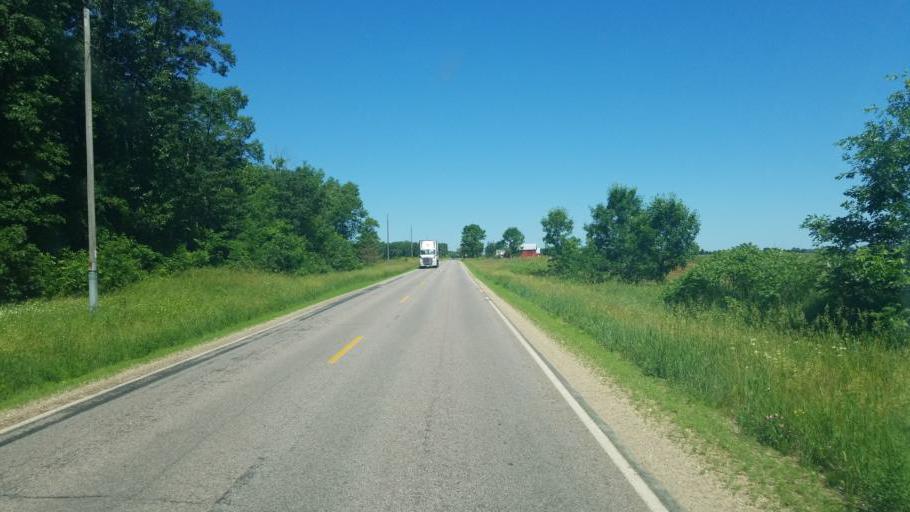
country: US
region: Wisconsin
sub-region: Adams County
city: Adams
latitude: 43.8216
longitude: -89.9043
